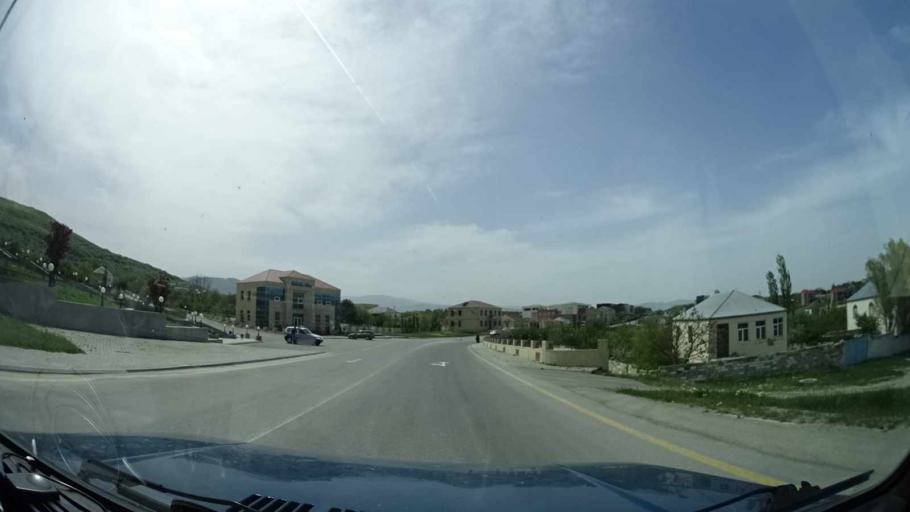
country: AZ
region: Xizi
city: Khyzy
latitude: 40.9101
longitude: 49.0769
